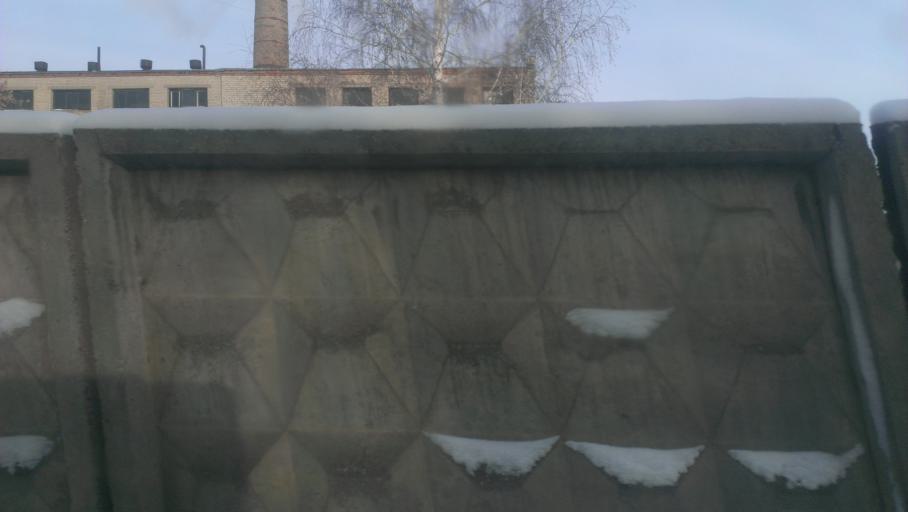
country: RU
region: Altai Krai
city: Nauchnyy Gorodok
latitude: 53.4217
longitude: 83.5209
